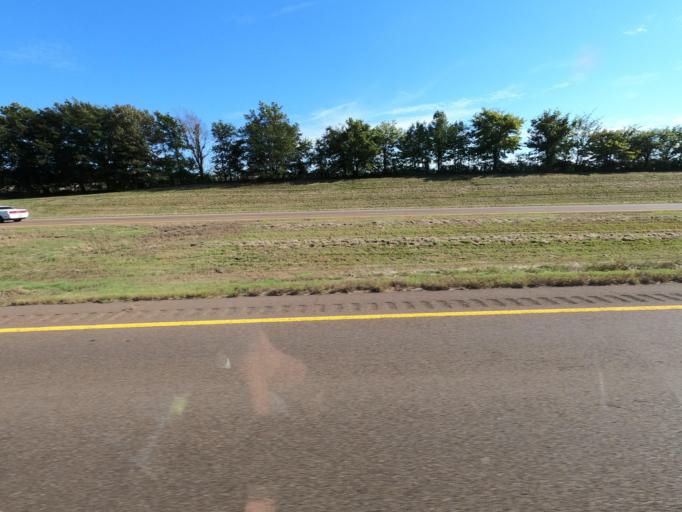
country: US
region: Tennessee
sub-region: Dyer County
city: Newbern
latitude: 36.1008
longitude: -89.3076
